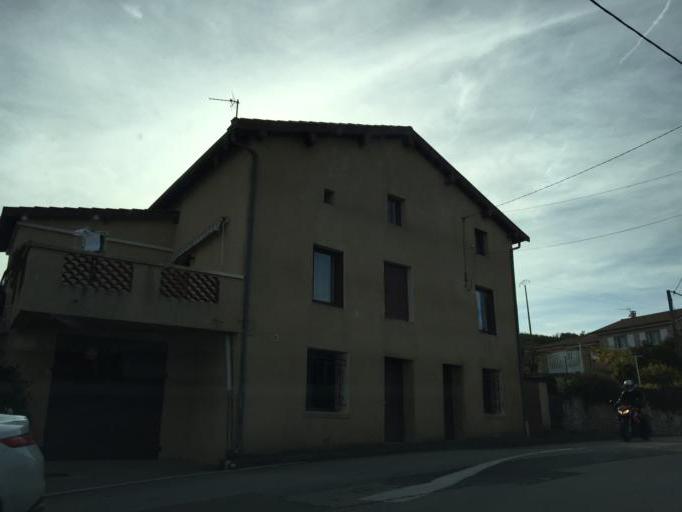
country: FR
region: Rhone-Alpes
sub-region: Departement de la Loire
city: Cellieu
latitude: 45.5284
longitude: 4.5637
